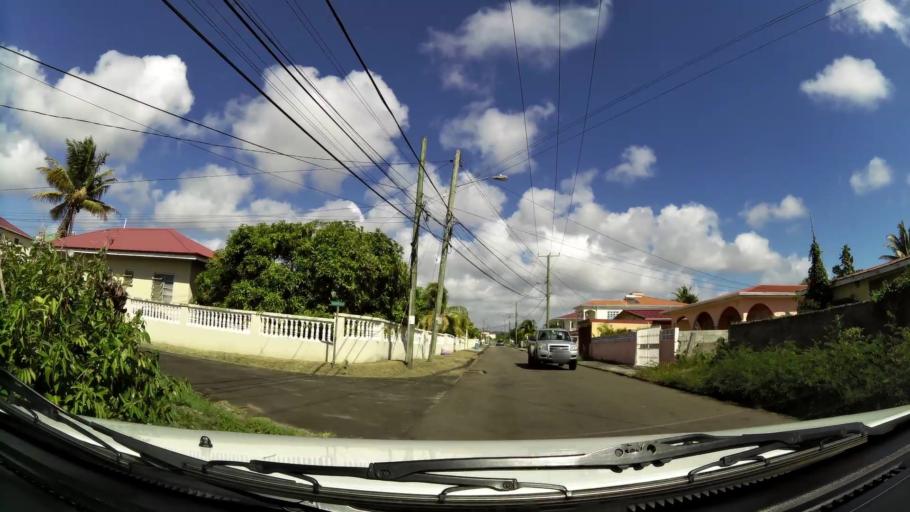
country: LC
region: Laborie Quarter
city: Laborie
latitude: 13.7444
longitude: -60.9760
